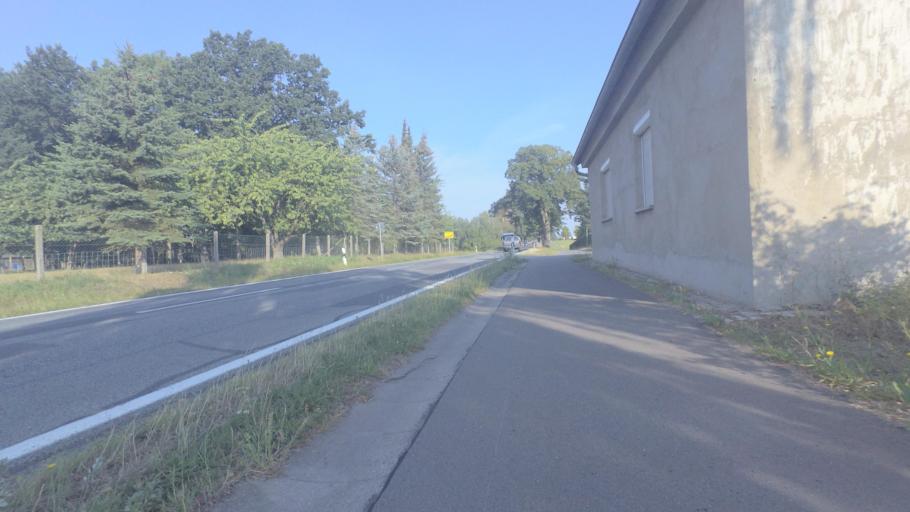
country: DE
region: Mecklenburg-Vorpommern
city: Grimmen
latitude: 54.0847
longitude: 13.0978
